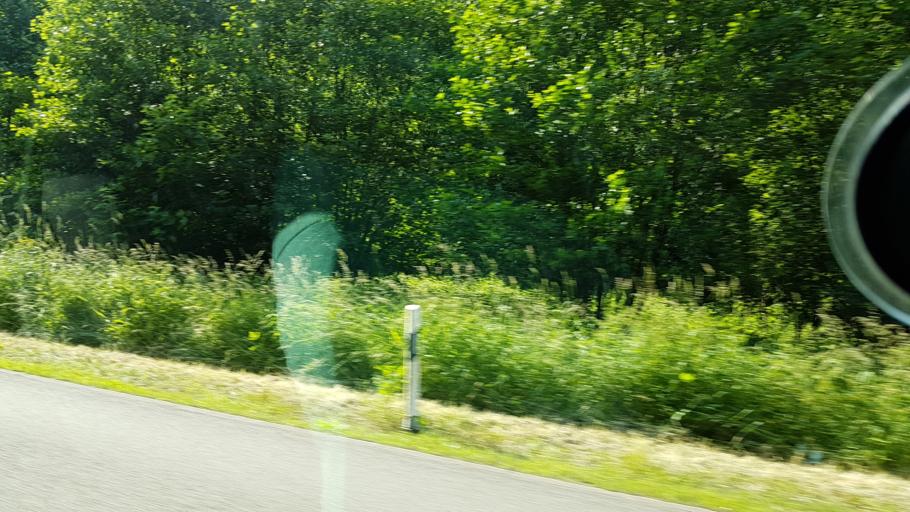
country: DE
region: Rheinland-Pfalz
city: Oberalben
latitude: 49.5998
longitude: 7.4002
